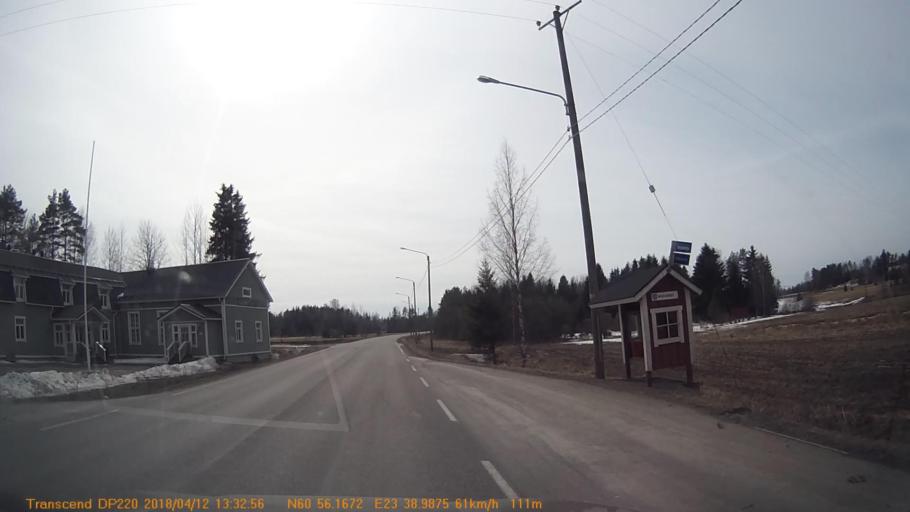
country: FI
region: Haeme
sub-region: Forssa
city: Forssa
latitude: 60.9360
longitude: 23.6497
